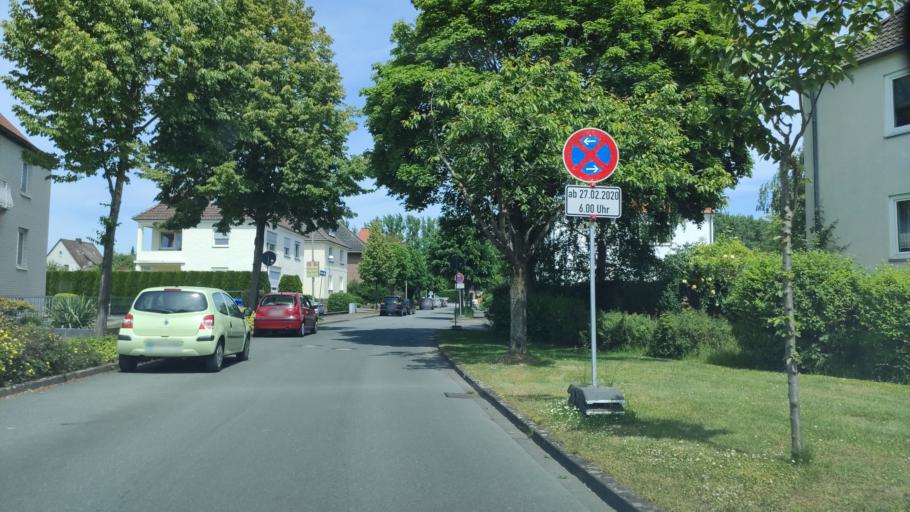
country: DE
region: North Rhine-Westphalia
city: Brakel
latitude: 51.7201
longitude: 9.1749
